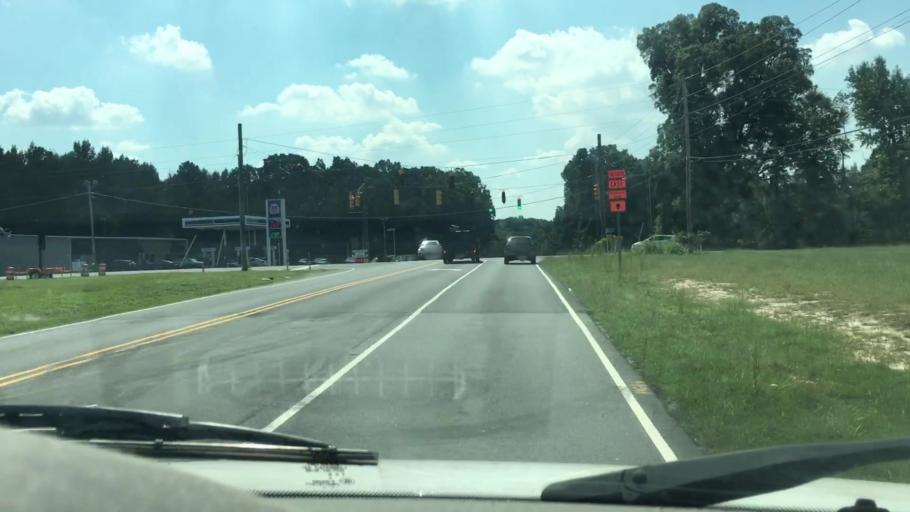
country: US
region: North Carolina
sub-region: Mecklenburg County
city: Huntersville
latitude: 35.3762
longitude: -80.8541
